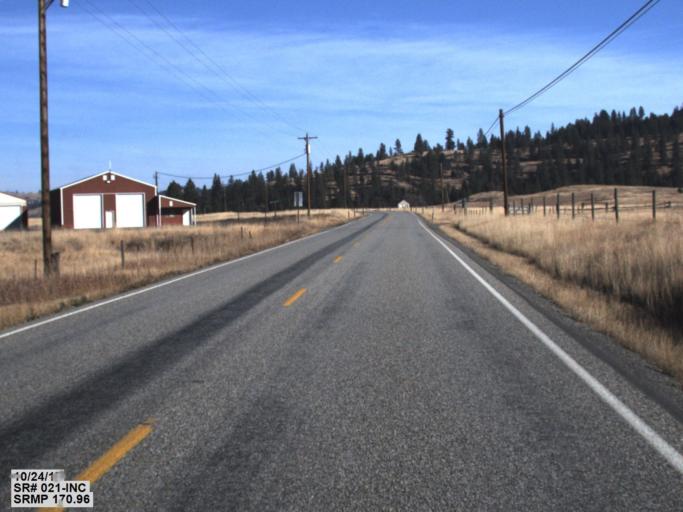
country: US
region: Washington
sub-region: Ferry County
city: Republic
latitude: 48.7555
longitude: -118.6490
